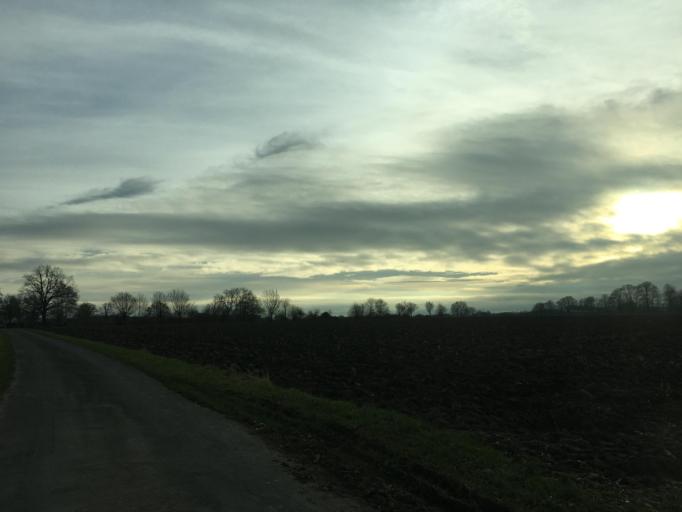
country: DE
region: North Rhine-Westphalia
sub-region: Regierungsbezirk Munster
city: Dulmen
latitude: 51.8339
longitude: 7.3298
